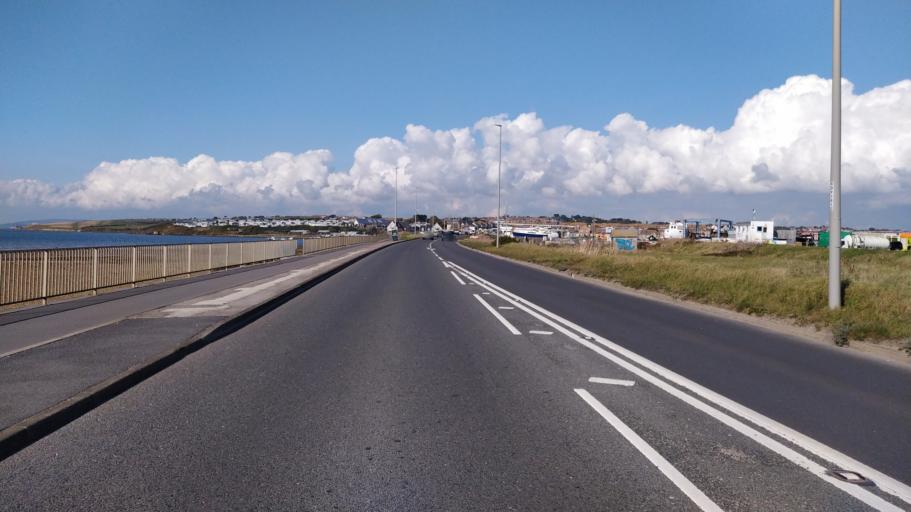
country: GB
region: England
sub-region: Dorset
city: Portland
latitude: 50.5805
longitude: -2.4701
